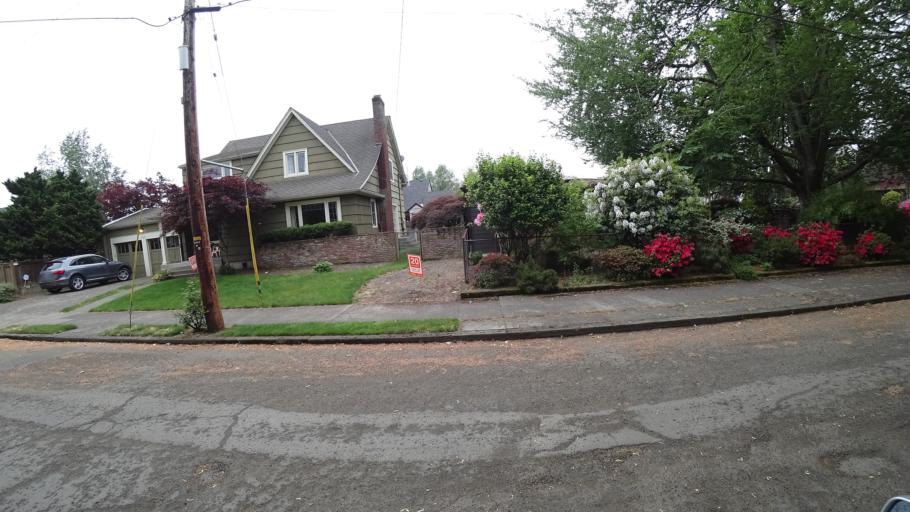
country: US
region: Oregon
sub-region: Multnomah County
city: Portland
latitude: 45.5473
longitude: -122.6263
